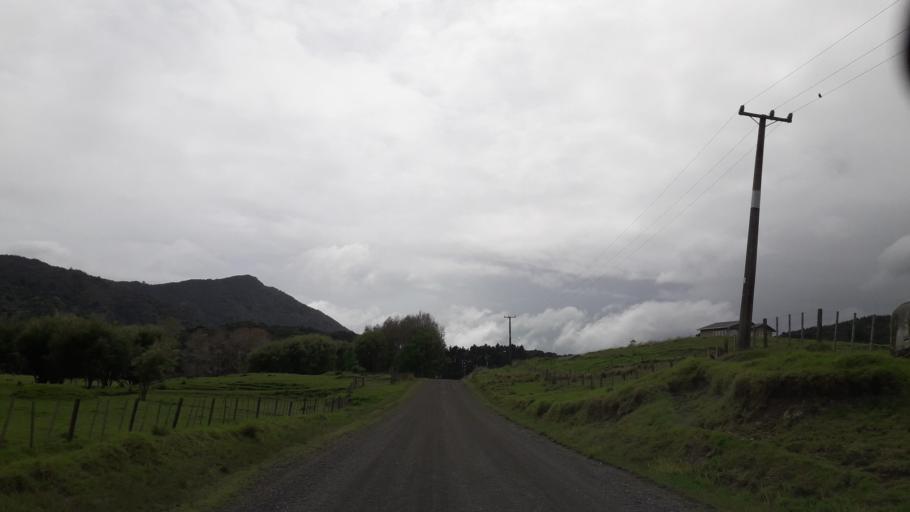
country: NZ
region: Northland
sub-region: Far North District
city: Ahipara
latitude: -35.4399
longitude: 173.3267
